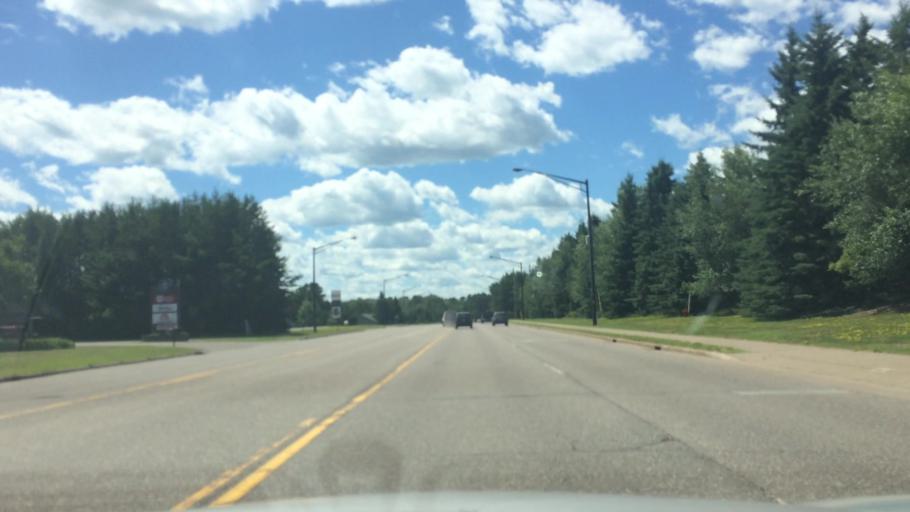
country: US
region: Wisconsin
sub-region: Vilas County
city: Lac du Flambeau
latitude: 45.8851
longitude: -89.7276
